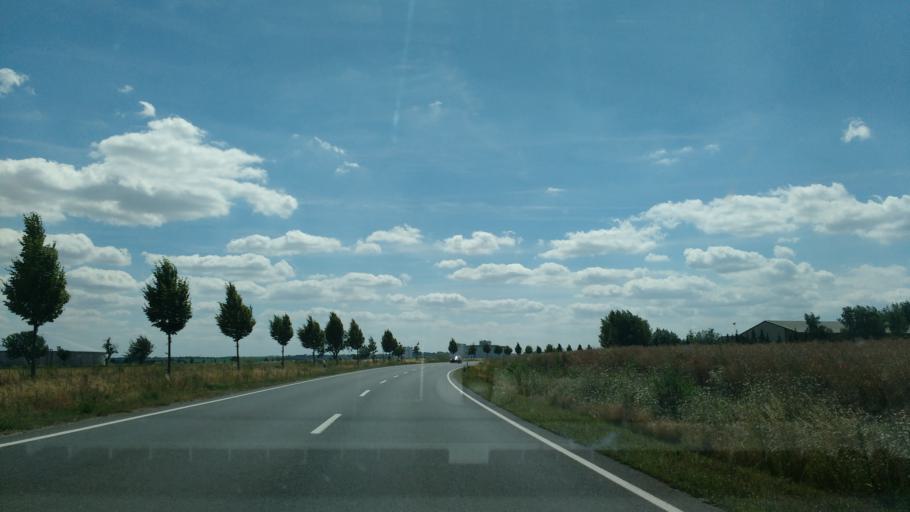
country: DE
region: Saxony-Anhalt
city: Querfurt
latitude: 51.4020
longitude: 11.6284
